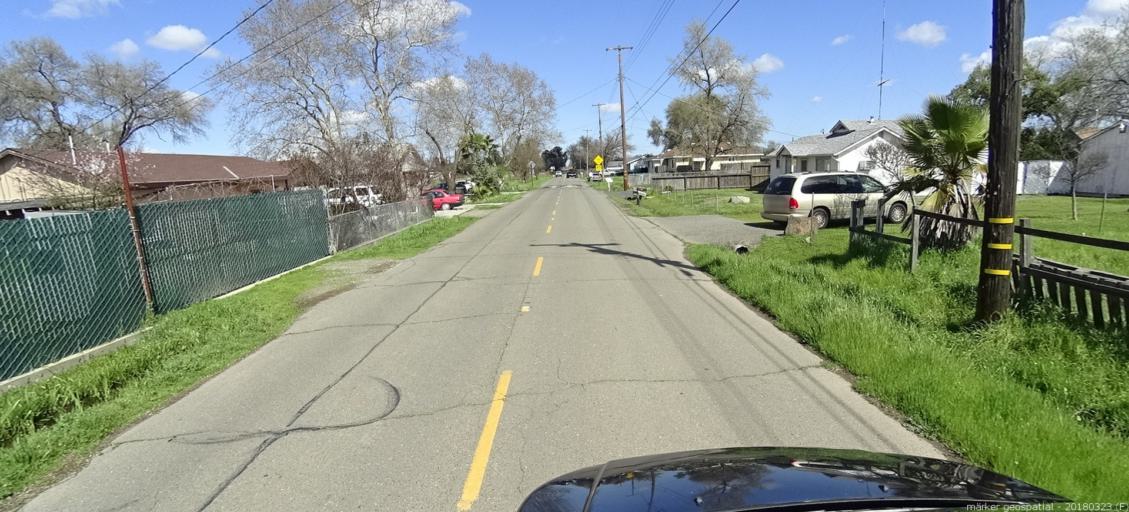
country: US
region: California
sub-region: Sacramento County
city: Rio Linda
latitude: 38.6810
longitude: -121.4153
